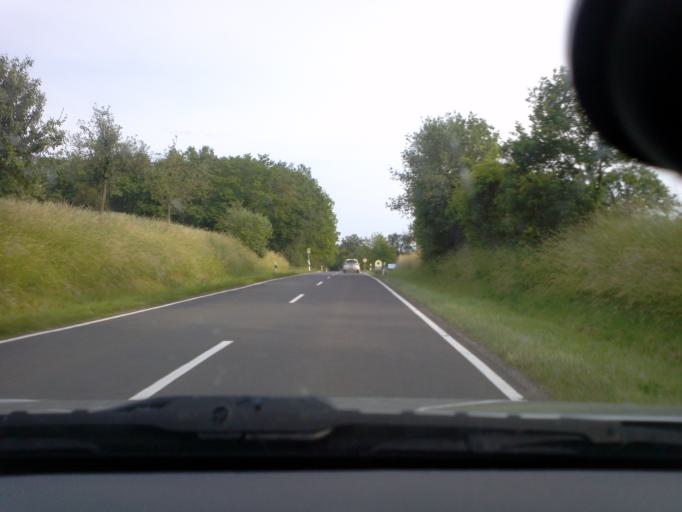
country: DE
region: Baden-Wuerttemberg
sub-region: Karlsruhe Region
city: Sternenfels
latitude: 49.0171
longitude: 8.8557
